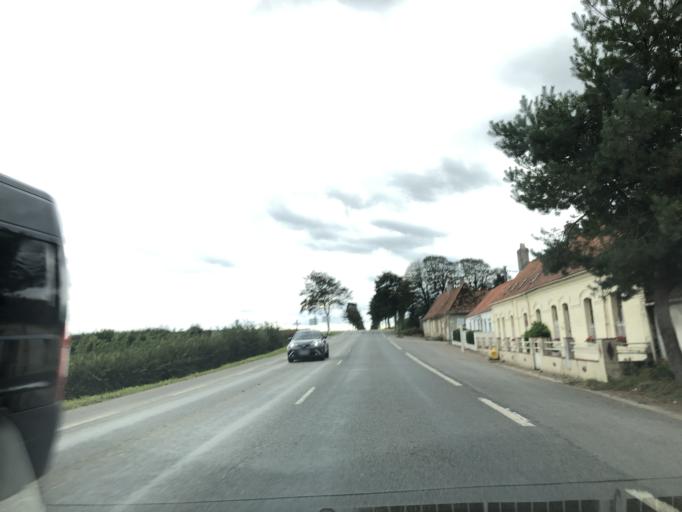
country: FR
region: Nord-Pas-de-Calais
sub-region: Departement du Pas-de-Calais
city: Auchy-les-Hesdin
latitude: 50.4560
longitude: 2.0928
